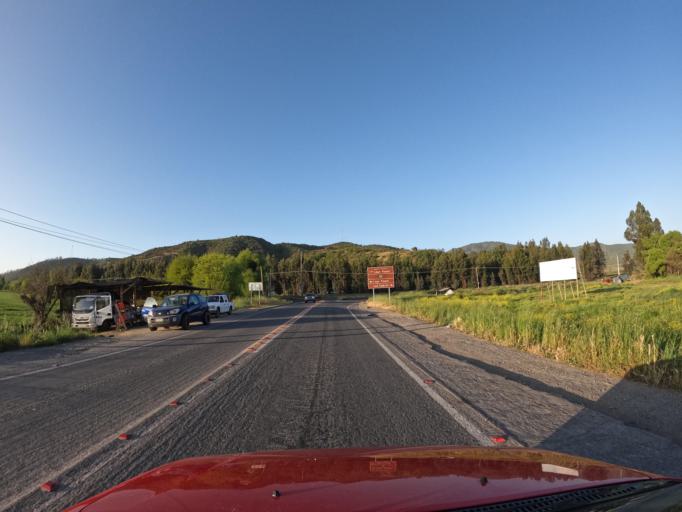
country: CL
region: O'Higgins
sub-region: Provincia de Cachapoal
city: San Vicente
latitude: -34.2727
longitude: -71.3624
